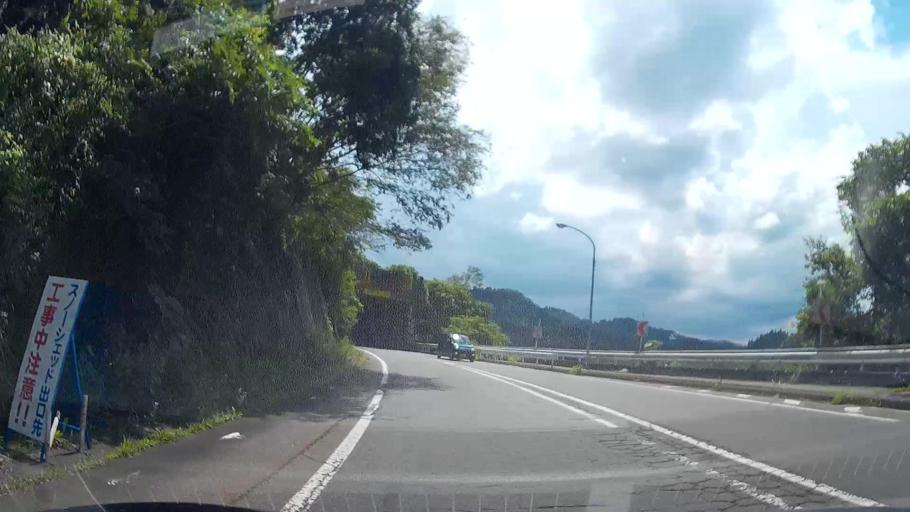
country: JP
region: Niigata
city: Tokamachi
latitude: 36.9989
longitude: 138.6171
